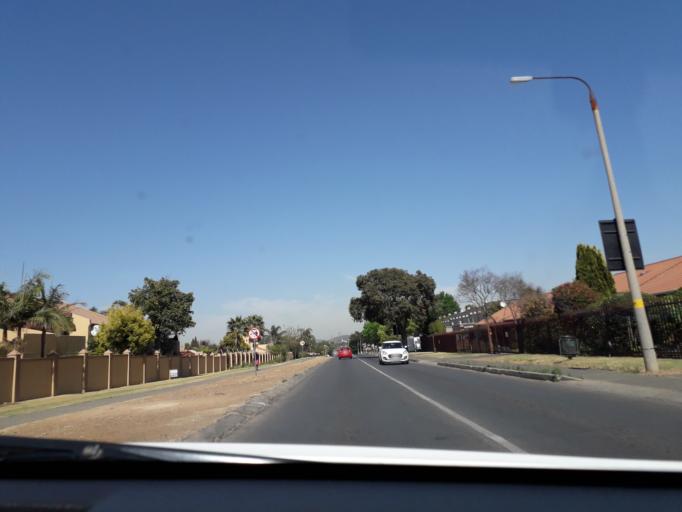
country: ZA
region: Gauteng
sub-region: City of Johannesburg Metropolitan Municipality
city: Modderfontein
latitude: -26.1365
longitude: 28.1785
